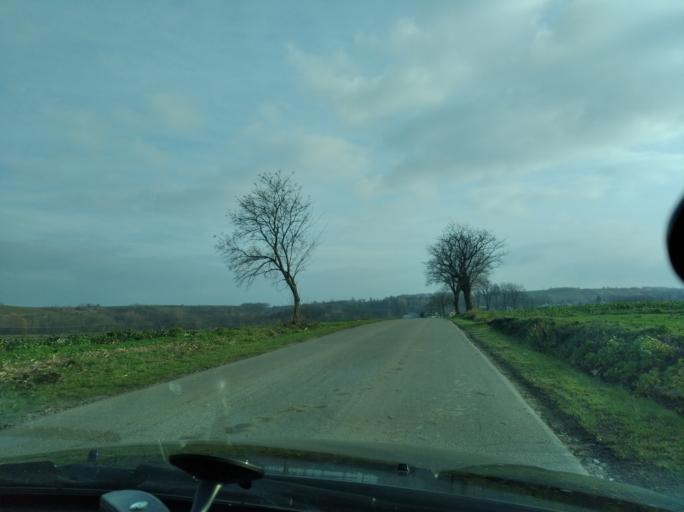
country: PL
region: Subcarpathian Voivodeship
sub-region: Powiat przeworski
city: Lopuszka Wielka
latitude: 49.9550
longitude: 22.4050
